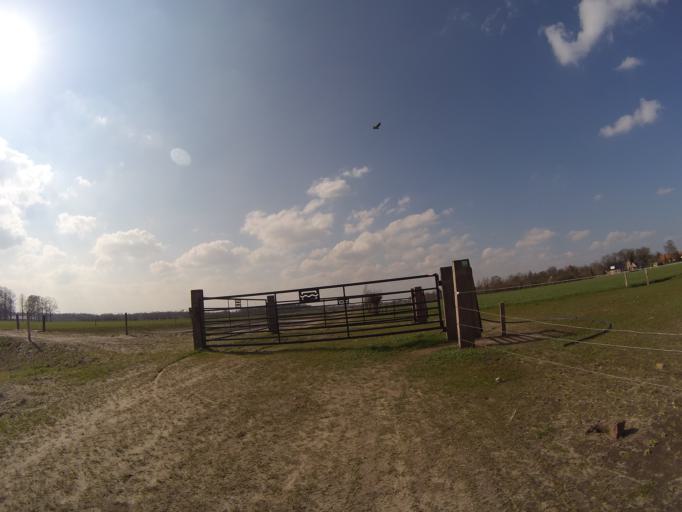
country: NL
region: Gelderland
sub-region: Gemeente Barneveld
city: Terschuur
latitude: 52.1318
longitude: 5.5042
